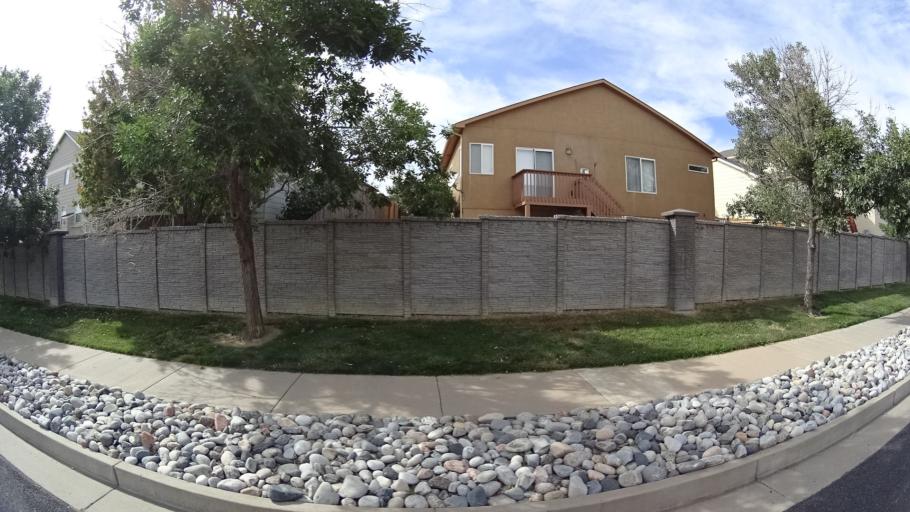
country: US
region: Colorado
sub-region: El Paso County
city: Cimarron Hills
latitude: 38.9038
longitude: -104.6850
